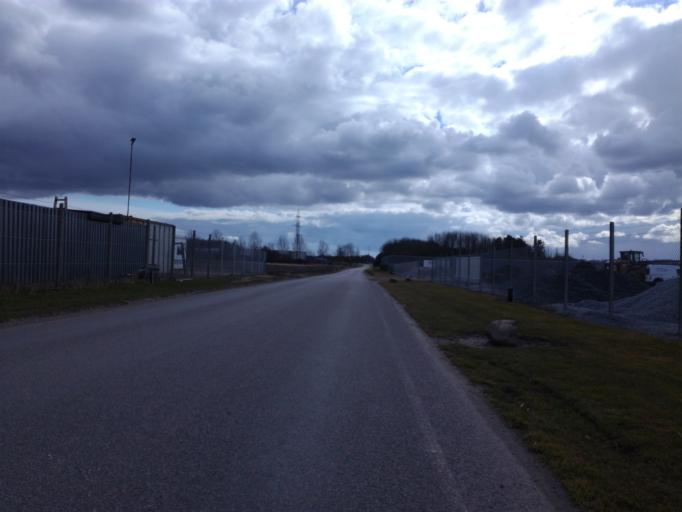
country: DK
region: South Denmark
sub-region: Fredericia Kommune
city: Fredericia
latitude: 55.5897
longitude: 9.7349
